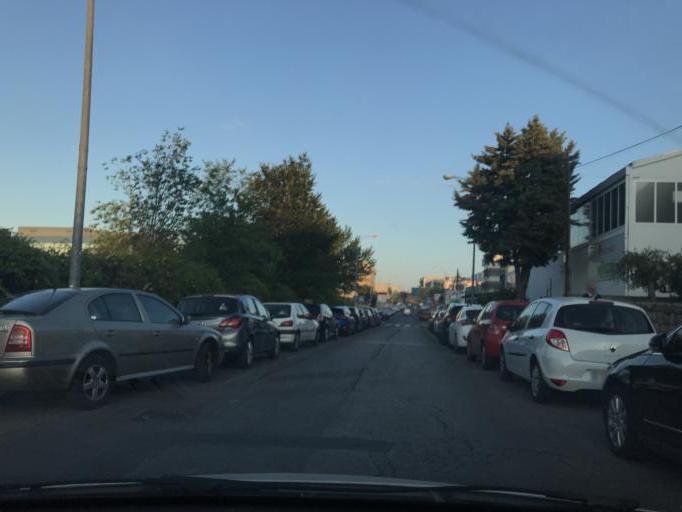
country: ES
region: Madrid
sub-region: Provincia de Madrid
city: Alcobendas
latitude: 40.5340
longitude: -3.6530
